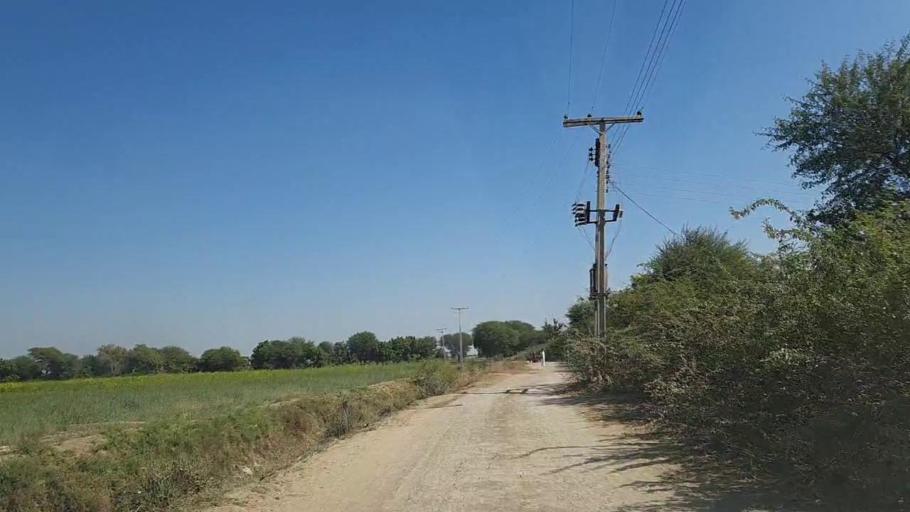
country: PK
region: Sindh
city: Naukot
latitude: 25.0370
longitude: 69.3898
